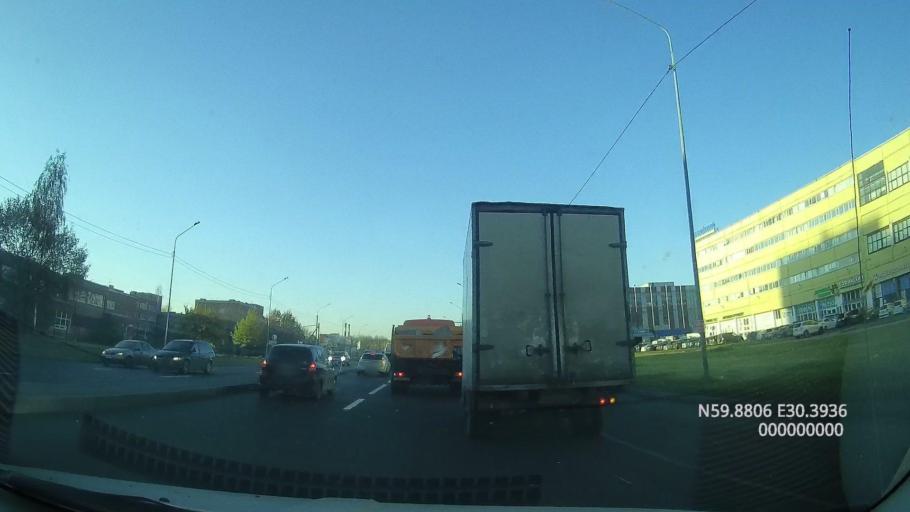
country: RU
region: St.-Petersburg
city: Kupchino
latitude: 59.8807
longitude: 30.3934
